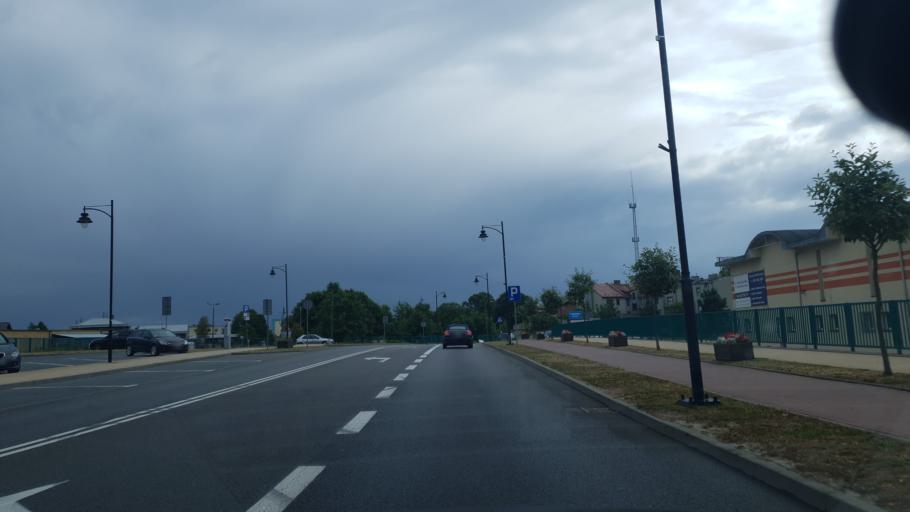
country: PL
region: Pomeranian Voivodeship
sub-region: Powiat kartuski
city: Kartuzy
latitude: 54.3332
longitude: 18.2049
